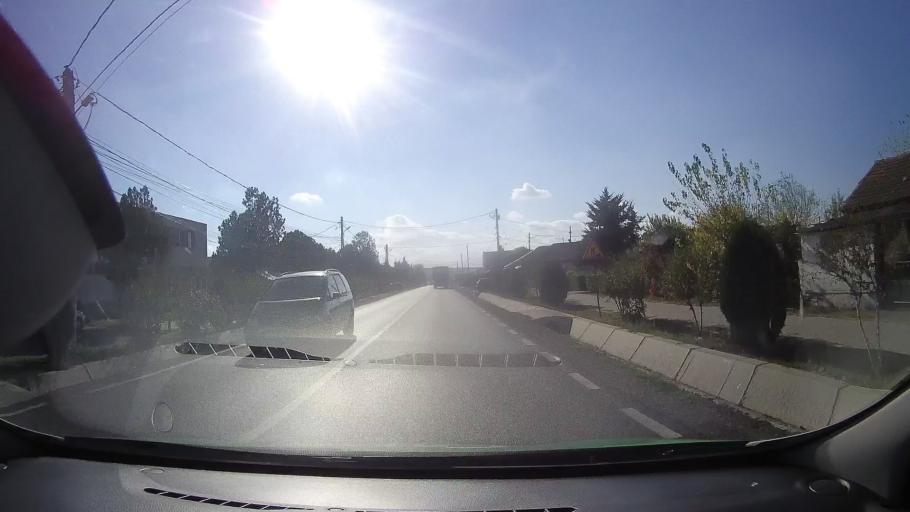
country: RO
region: Tulcea
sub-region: Comuna Baia
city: Baia
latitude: 44.7270
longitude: 28.6806
